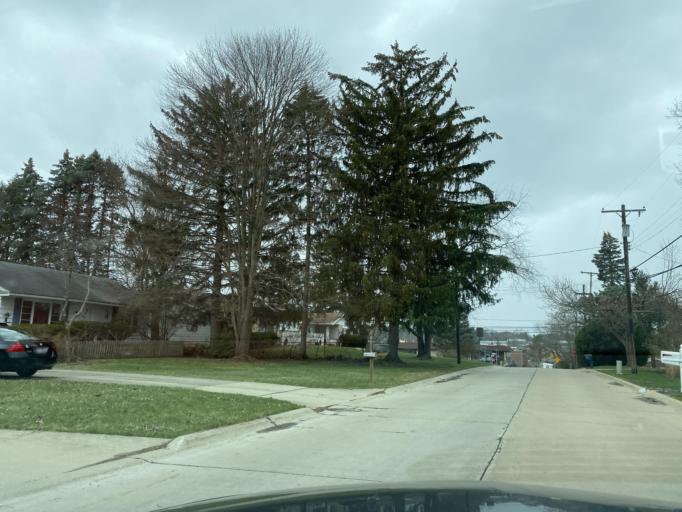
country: US
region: Ohio
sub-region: Summit County
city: Fairlawn
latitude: 41.1291
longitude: -81.6059
